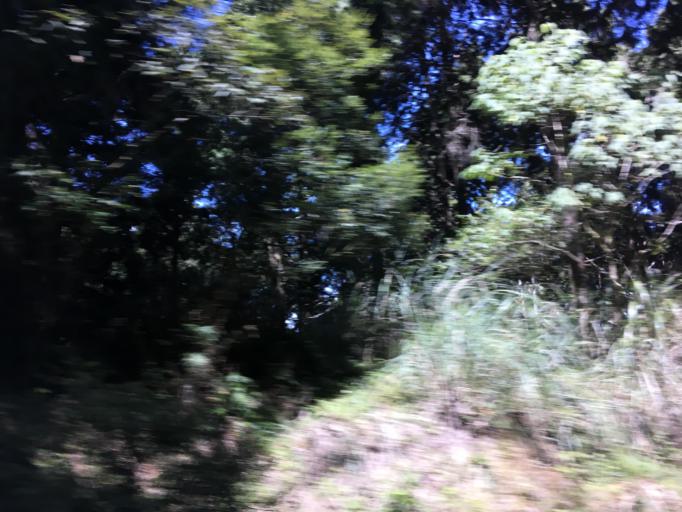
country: TW
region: Taiwan
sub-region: Yilan
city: Yilan
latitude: 24.5121
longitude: 121.5215
